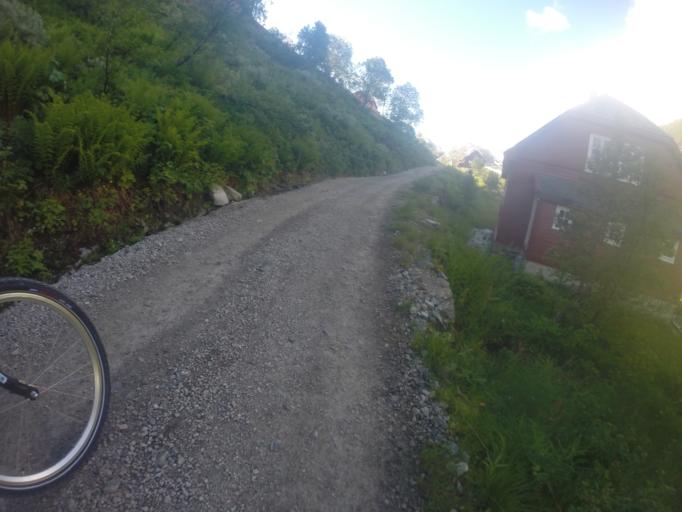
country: NO
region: Sogn og Fjordane
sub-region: Aurland
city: Aurlandsvangen
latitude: 60.7369
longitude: 7.1219
